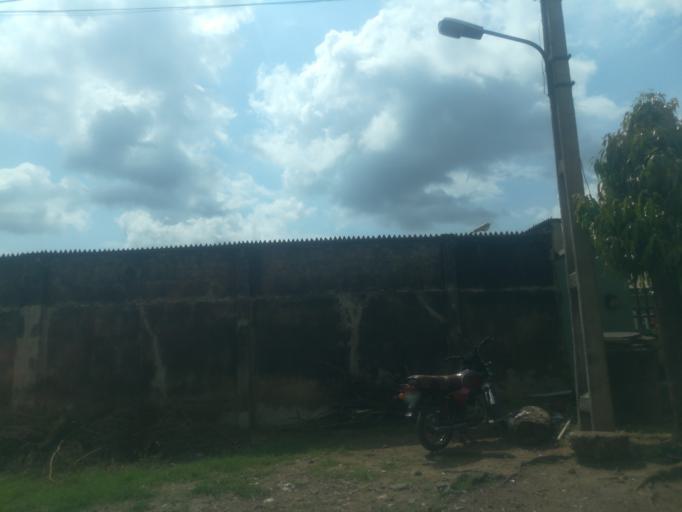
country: NG
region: Oyo
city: Ibadan
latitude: 7.3622
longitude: 3.8542
